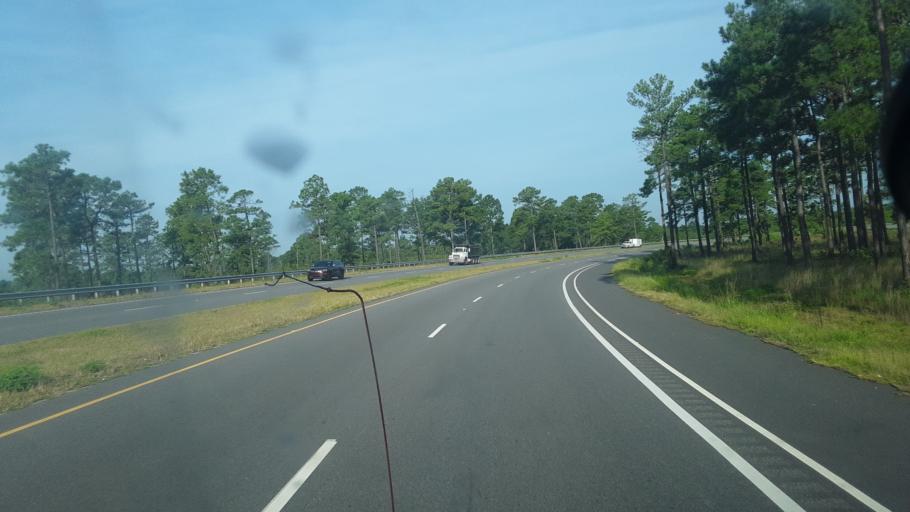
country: US
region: South Carolina
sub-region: Horry County
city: Forestbrook
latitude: 33.8174
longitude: -78.9102
